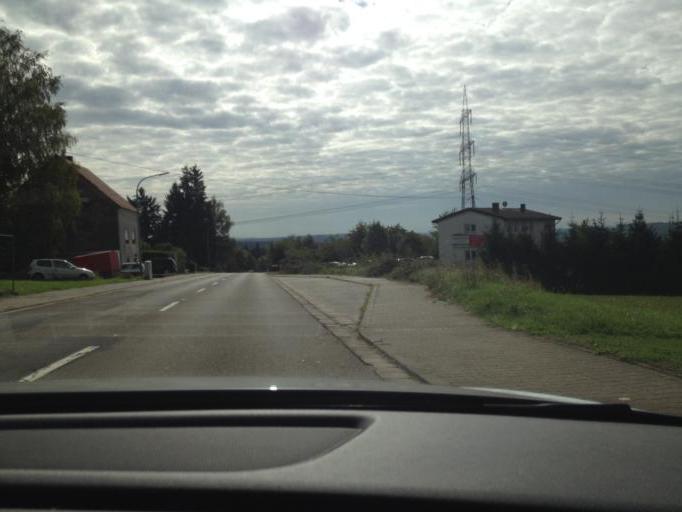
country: DE
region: Saarland
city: Schiffweiler
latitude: 49.3819
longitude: 7.1190
